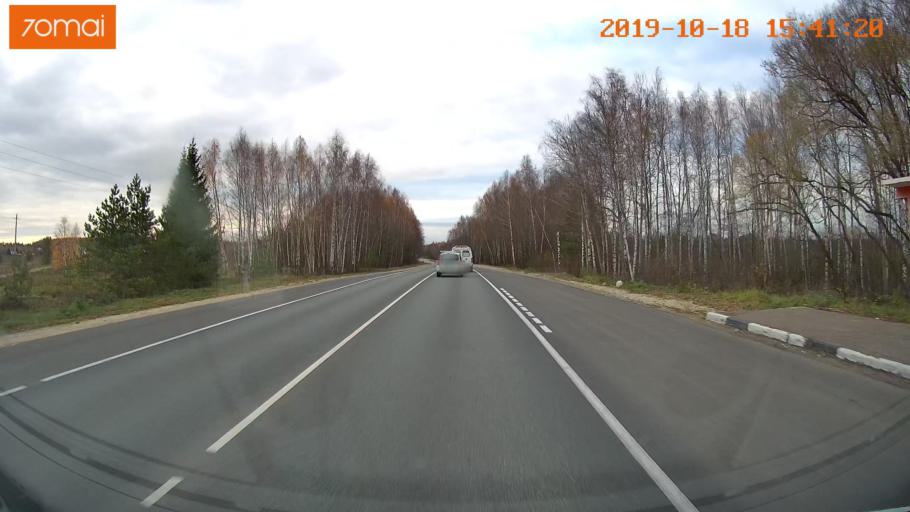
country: RU
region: Vladimir
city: Golovino
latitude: 55.9444
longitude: 40.5843
